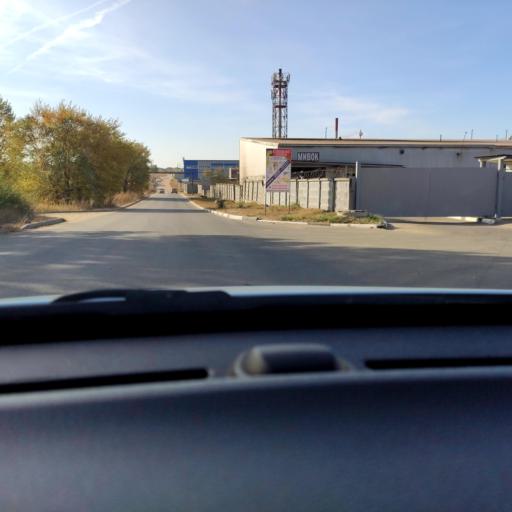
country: RU
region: Voronezj
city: Pridonskoy
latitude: 51.6406
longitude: 39.1106
